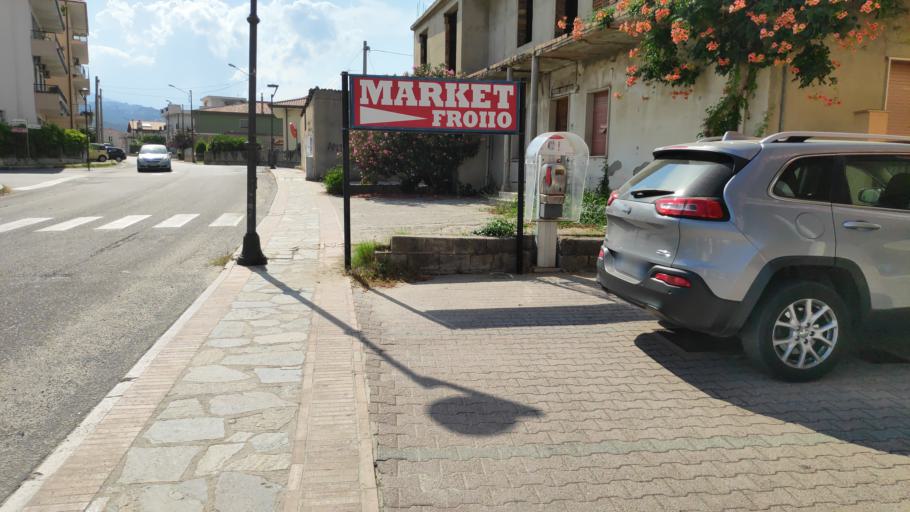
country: IT
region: Calabria
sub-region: Provincia di Catanzaro
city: Marina di Davoli
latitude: 38.6677
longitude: 16.5424
